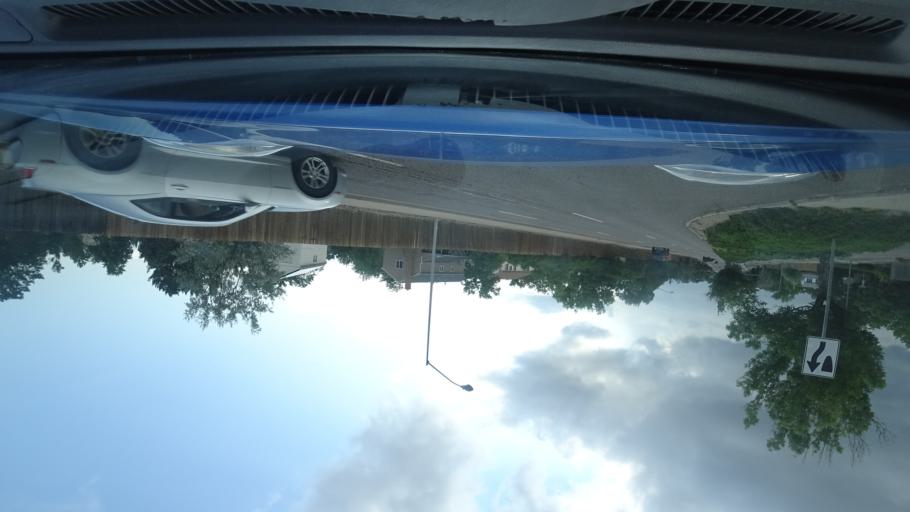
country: US
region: Colorado
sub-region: Adams County
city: Aurora
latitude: 39.6966
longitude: -104.8000
